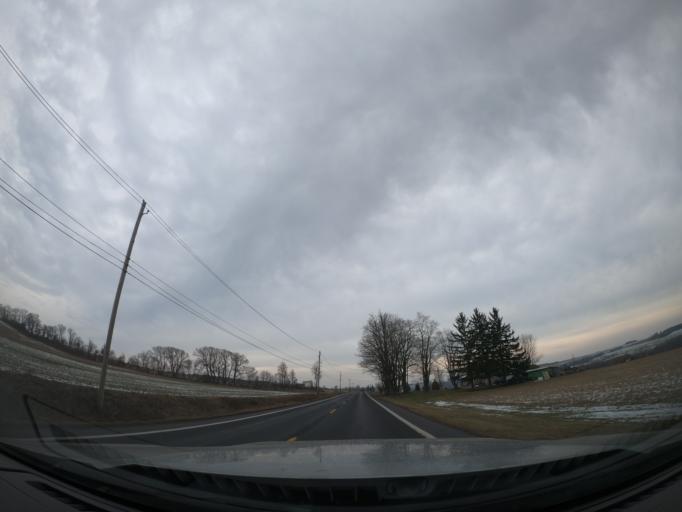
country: US
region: New York
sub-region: Cayuga County
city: Moravia
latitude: 42.7568
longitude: -76.5566
